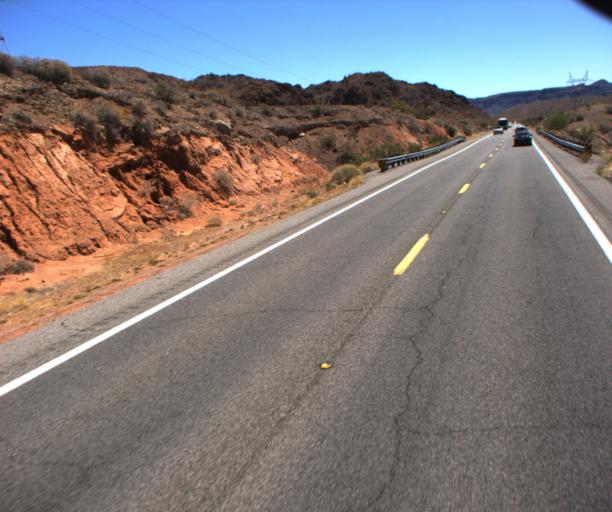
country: US
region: Arizona
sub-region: La Paz County
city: Cienega Springs
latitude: 34.3361
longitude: -114.1390
